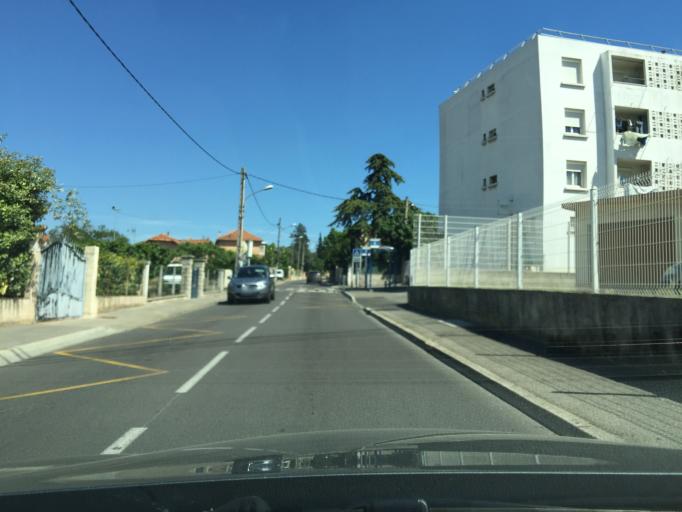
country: FR
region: Provence-Alpes-Cote d'Azur
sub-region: Departement des Bouches-du-Rhone
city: La Penne-sur-Huveaune
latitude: 43.2784
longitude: 5.5178
